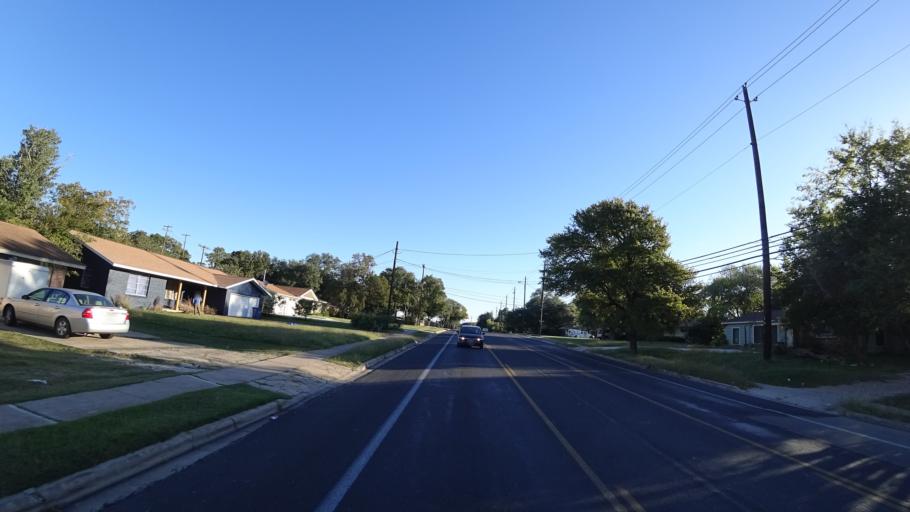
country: US
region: Texas
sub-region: Travis County
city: Austin
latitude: 30.3025
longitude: -97.6835
